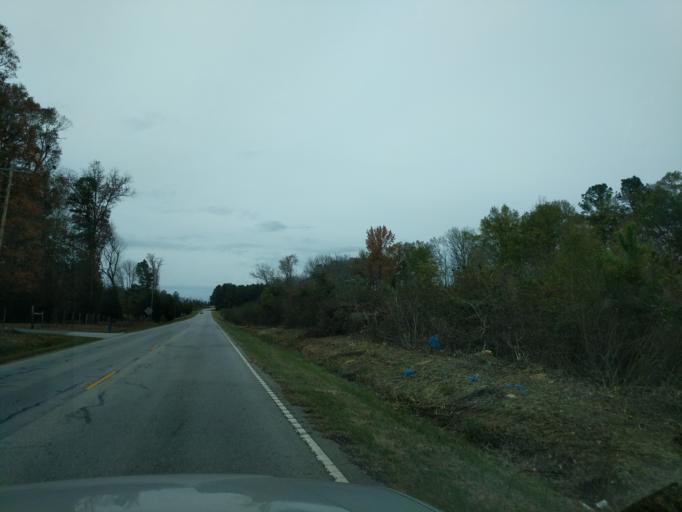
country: US
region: South Carolina
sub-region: Saluda County
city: Saluda
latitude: 34.0320
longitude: -81.7692
